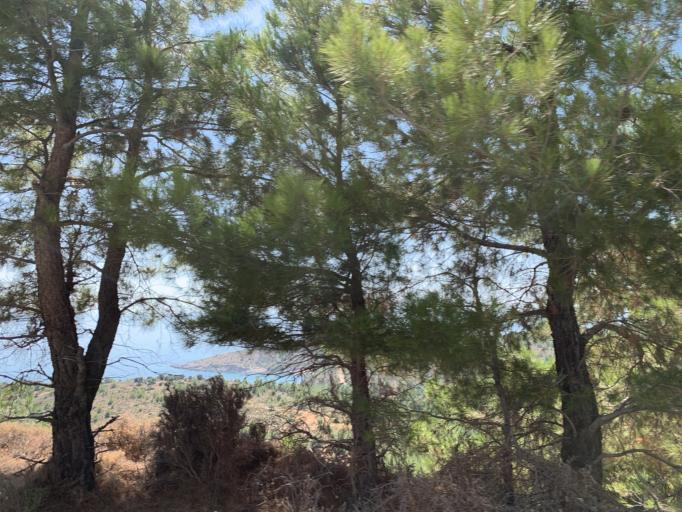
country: GR
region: North Aegean
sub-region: Chios
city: Vrontados
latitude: 38.4048
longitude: 25.9733
